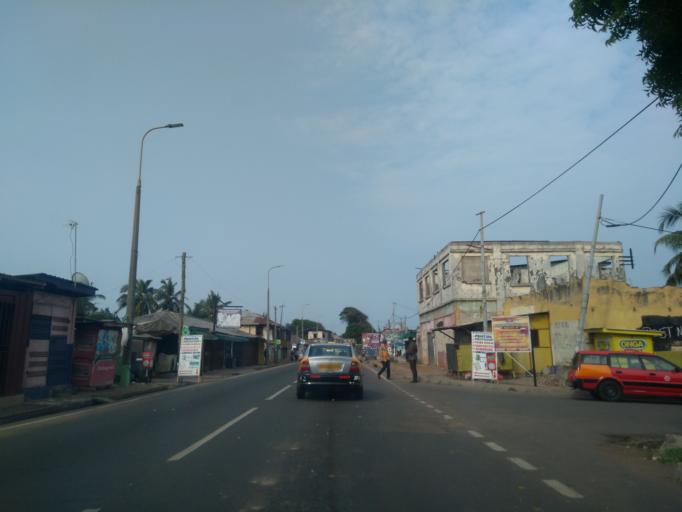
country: GH
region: Greater Accra
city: Accra
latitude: 5.5502
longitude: -0.1865
